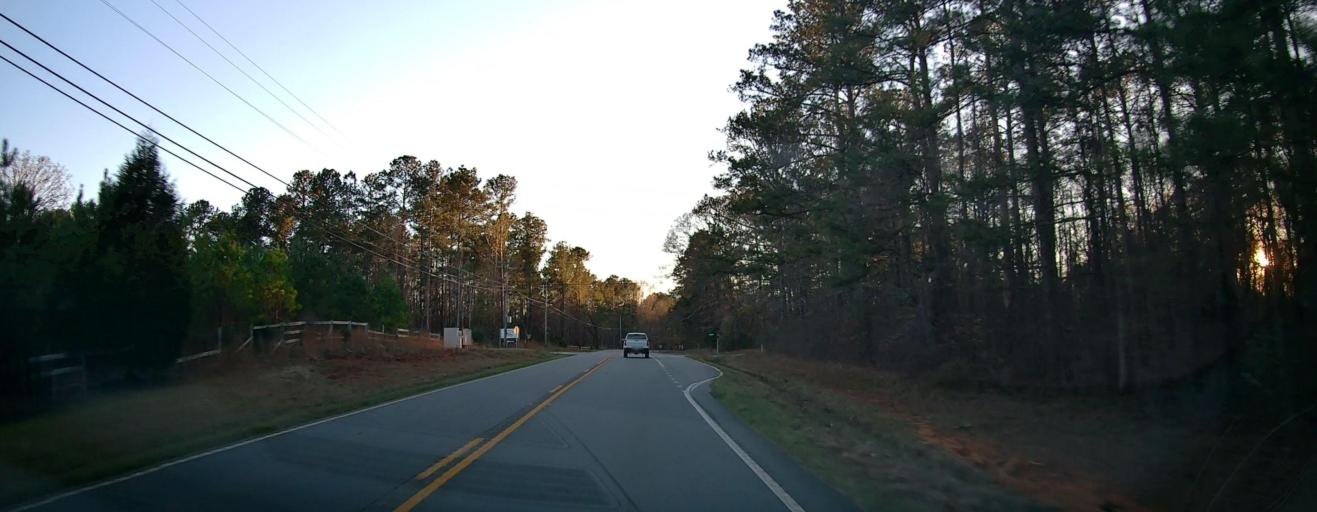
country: US
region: Alabama
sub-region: Lee County
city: Smiths Station
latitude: 32.6413
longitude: -85.0226
